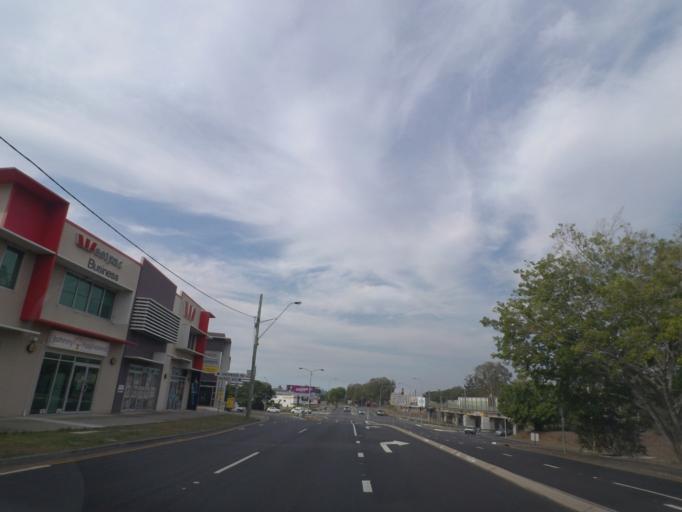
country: AU
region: Queensland
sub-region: Brisbane
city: Rocklea
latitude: -27.5423
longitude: 153.0113
